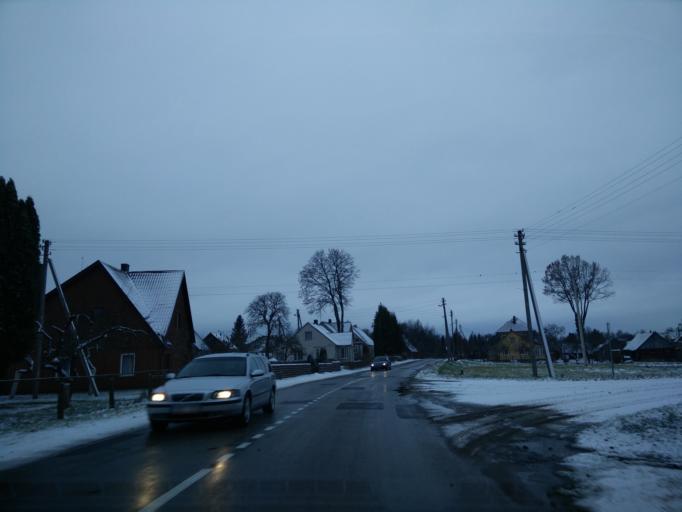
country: LT
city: Tytuveneliai
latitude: 55.5271
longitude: 23.2324
